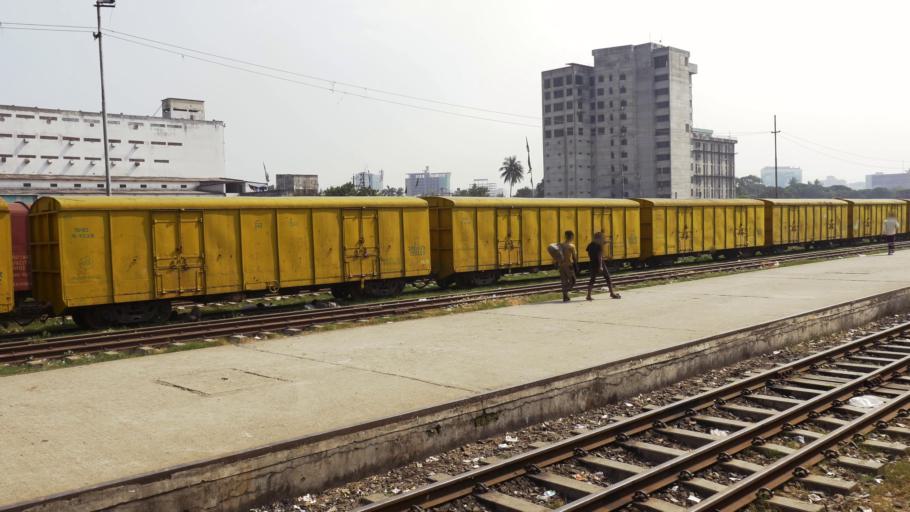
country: BD
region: Dhaka
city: Paltan
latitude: 23.7713
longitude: 90.3967
